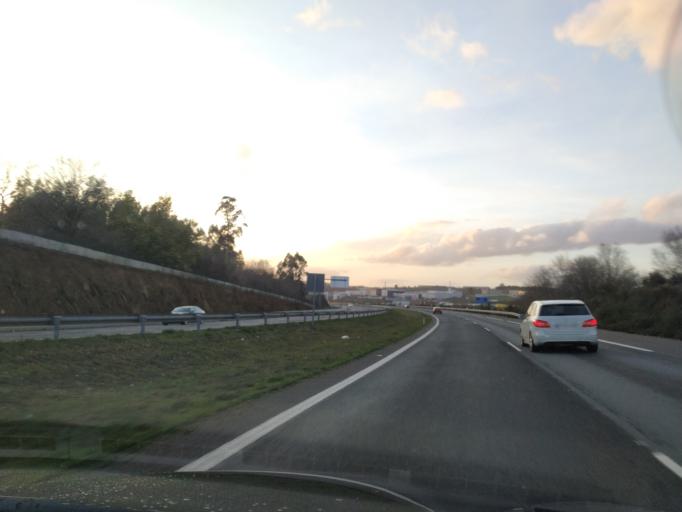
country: ES
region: Galicia
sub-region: Provincia da Coruna
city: Santiago de Compostela
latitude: 42.9004
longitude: -8.4912
